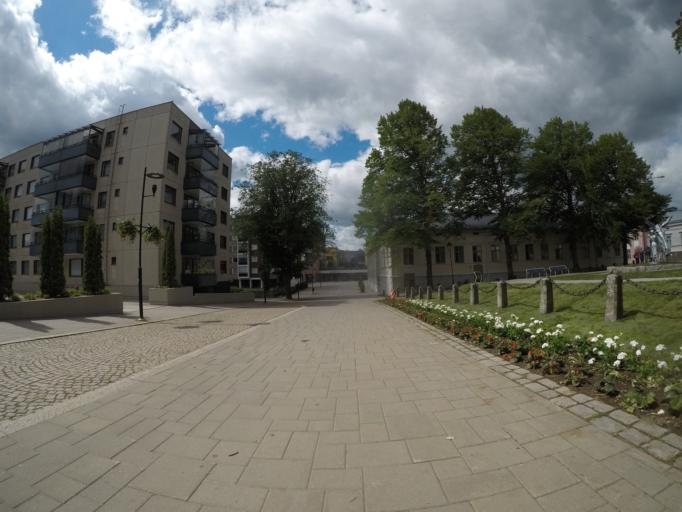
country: FI
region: Haeme
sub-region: Haemeenlinna
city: Haemeenlinna
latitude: 60.9950
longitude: 24.4594
